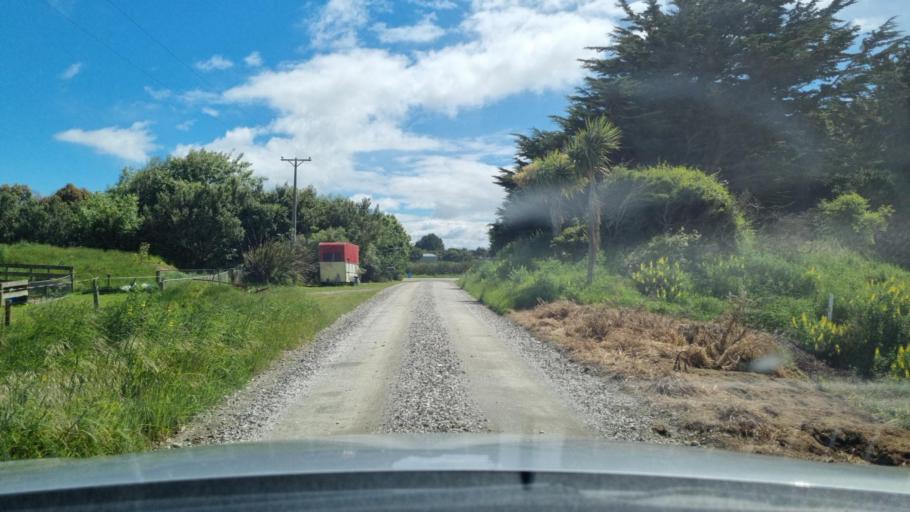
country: NZ
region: Southland
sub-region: Invercargill City
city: Invercargill
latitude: -46.4537
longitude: 168.2813
